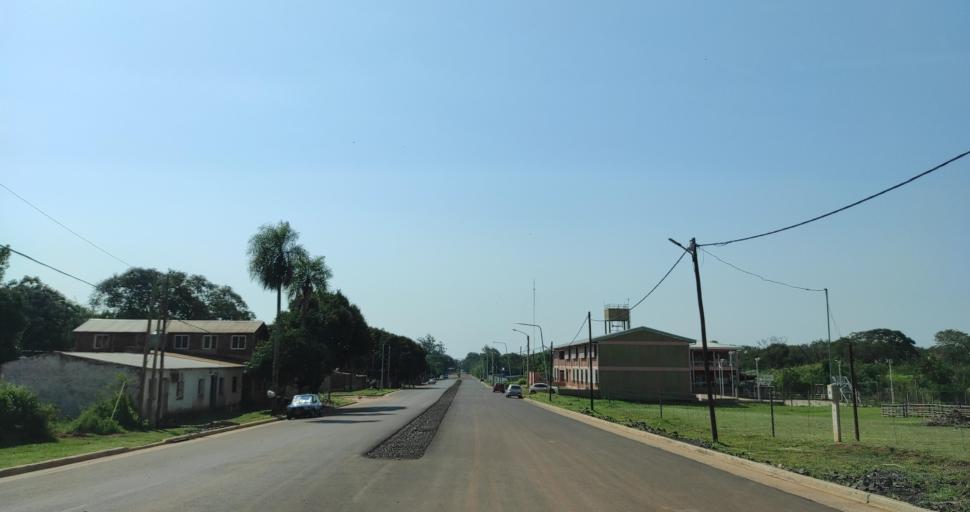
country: AR
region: Misiones
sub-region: Departamento de Capital
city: Posadas
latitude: -27.3609
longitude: -55.9270
